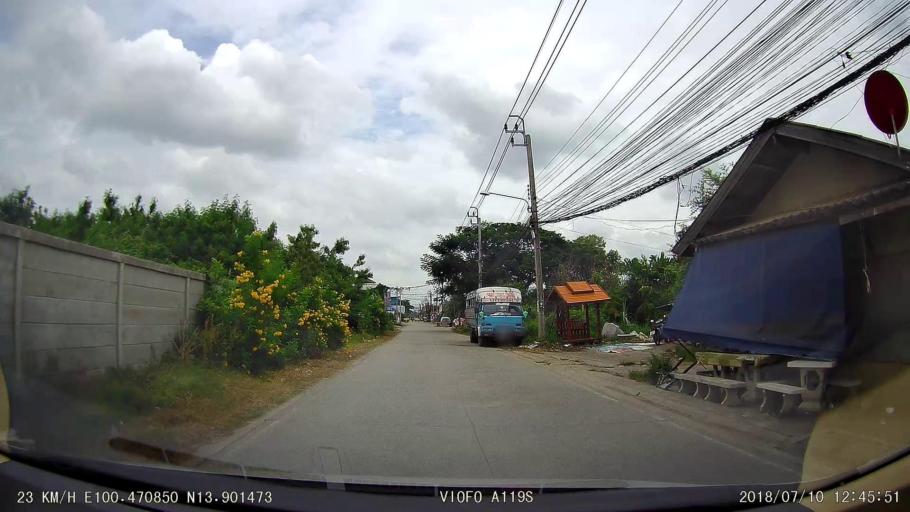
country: TH
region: Nonthaburi
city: Pak Kret
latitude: 13.9014
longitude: 100.4708
